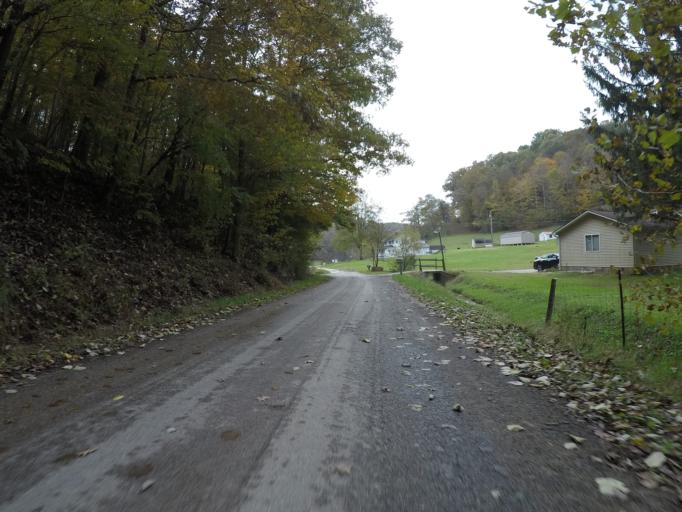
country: US
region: West Virginia
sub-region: Wayne County
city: Lavalette
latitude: 38.3491
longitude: -82.4217
